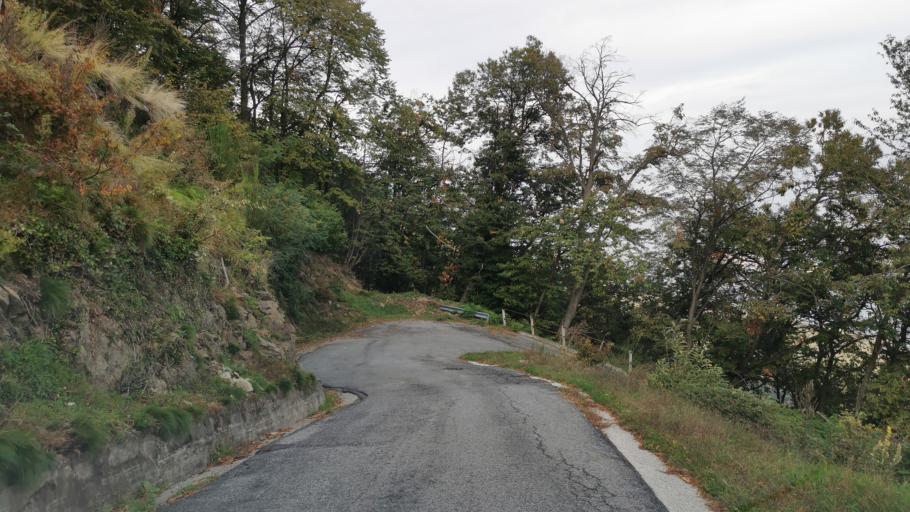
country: IT
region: Lombardy
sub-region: Provincia di Como
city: San Siro
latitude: 46.0670
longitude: 9.2558
